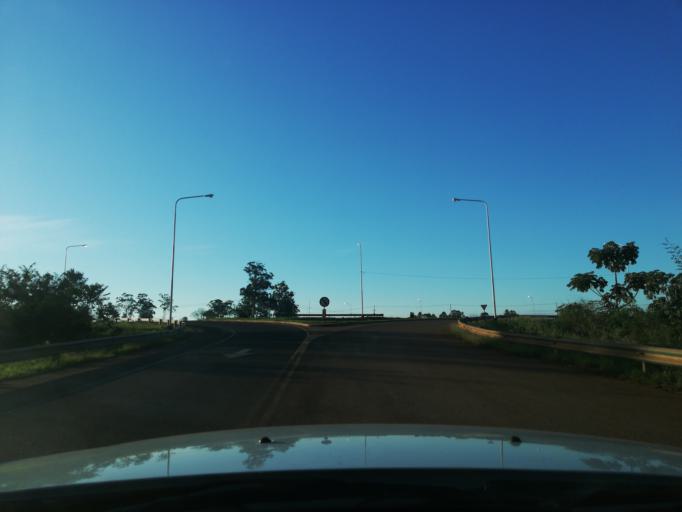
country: AR
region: Misiones
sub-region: Departamento de Capital
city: Posadas
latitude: -27.4662
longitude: -55.9708
